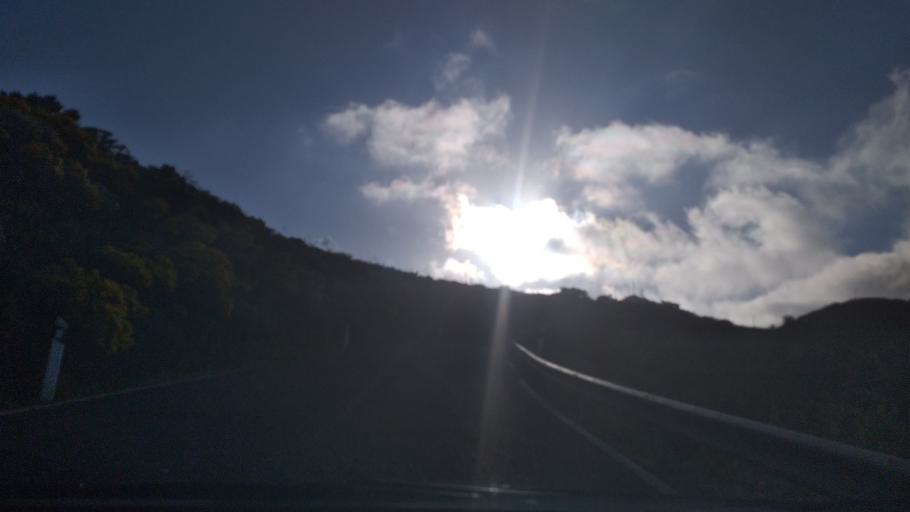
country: ES
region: Canary Islands
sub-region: Provincia de Las Palmas
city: Valsequillo de Gran Canaria
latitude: 27.9573
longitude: -15.4958
